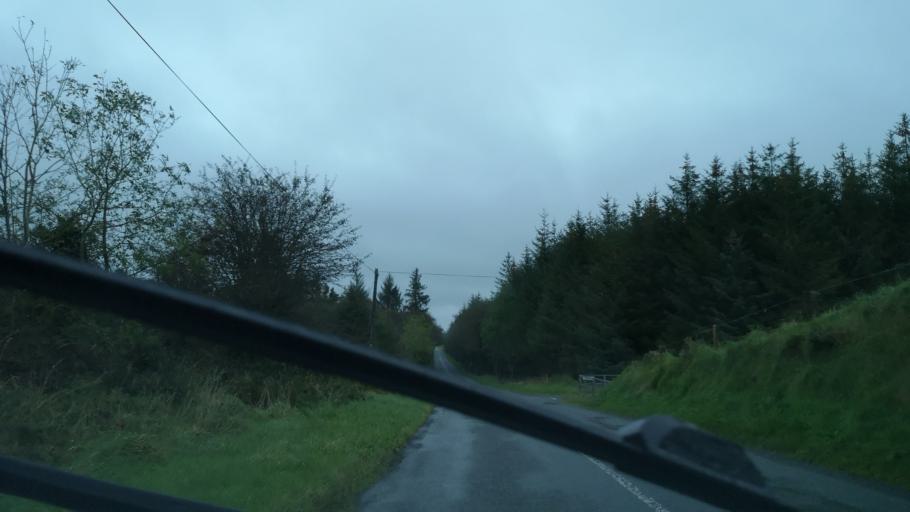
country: IE
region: Connaught
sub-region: Maigh Eo
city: Ballyhaunis
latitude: 53.7935
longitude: -8.7078
